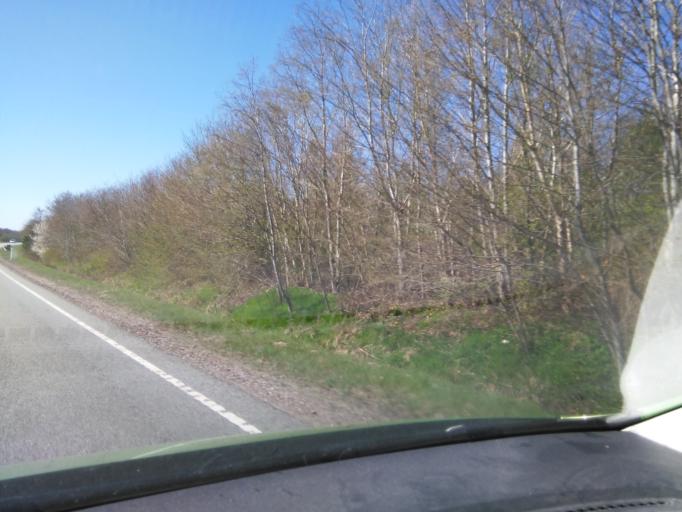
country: DK
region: South Denmark
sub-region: Varde Kommune
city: Varde
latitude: 55.6458
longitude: 8.5367
